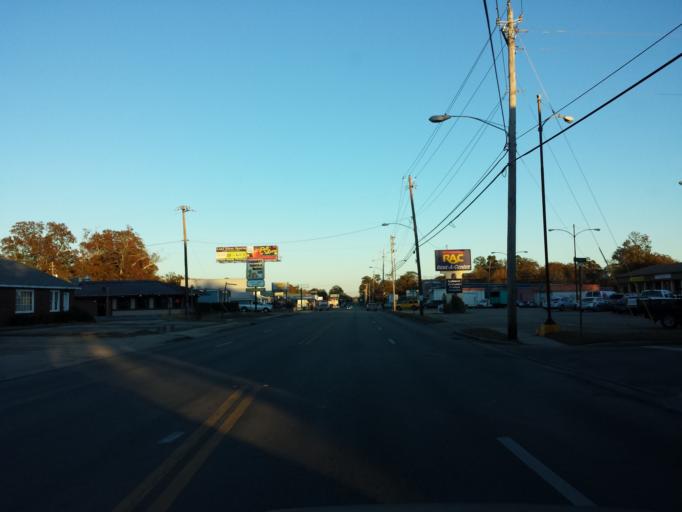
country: US
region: Mississippi
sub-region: Forrest County
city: Hattiesburg
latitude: 31.3247
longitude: -89.3095
